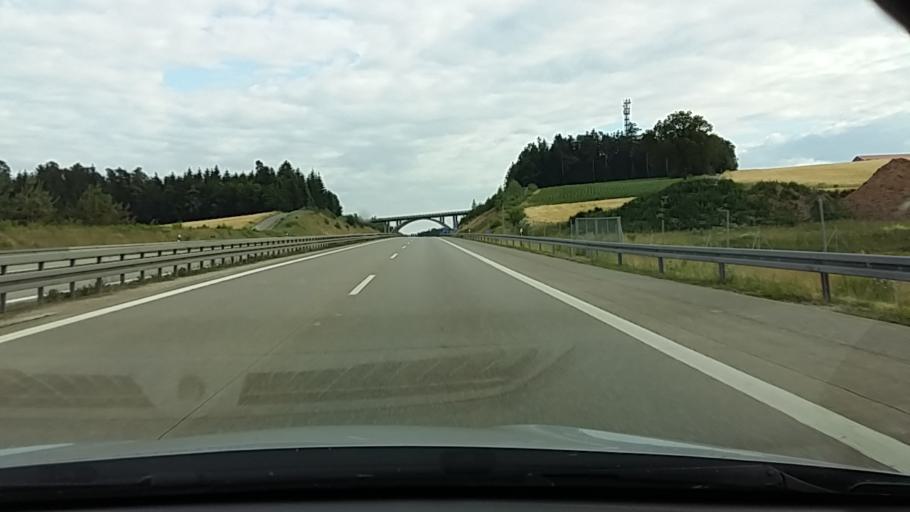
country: DE
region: Bavaria
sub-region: Upper Palatinate
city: Nabburg
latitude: 49.4731
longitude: 12.1349
